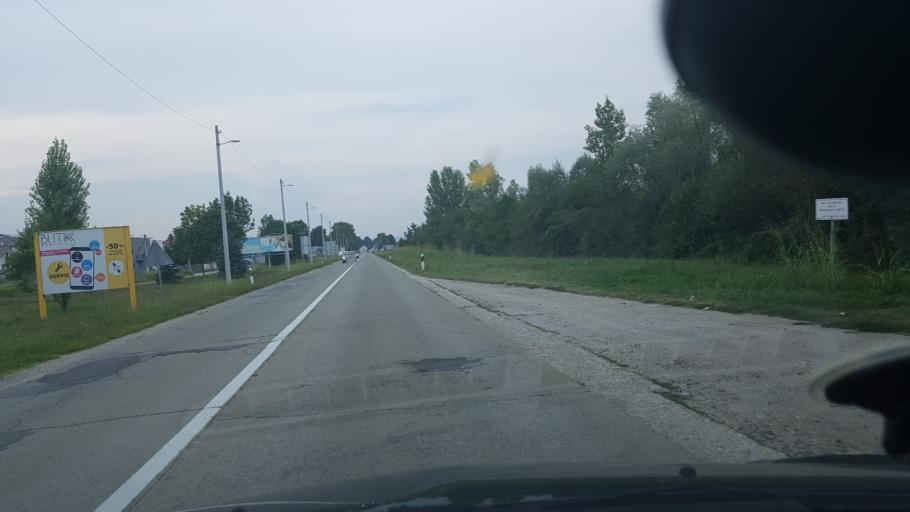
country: HR
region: Zagrebacka
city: Bregana
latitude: 45.8267
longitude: 15.7021
